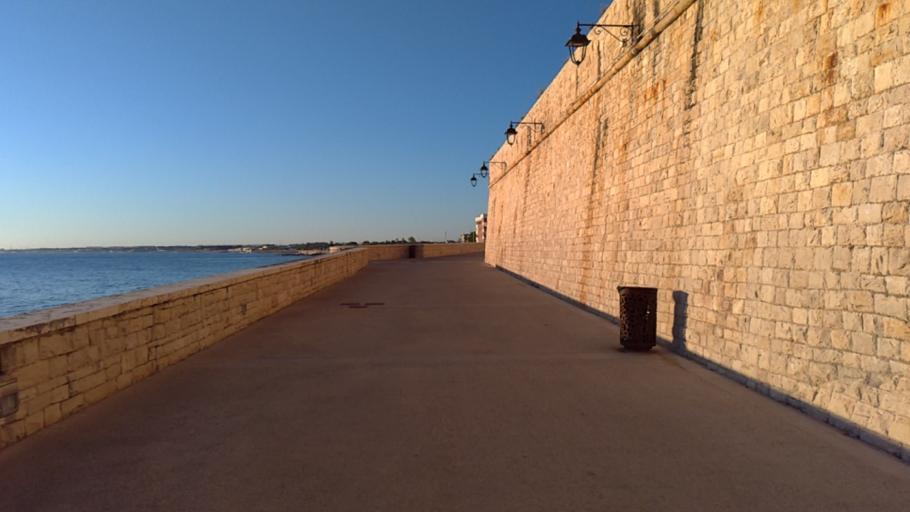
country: IT
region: Apulia
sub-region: Provincia di Bari
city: Giovinazzo
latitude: 41.1888
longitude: 16.6750
